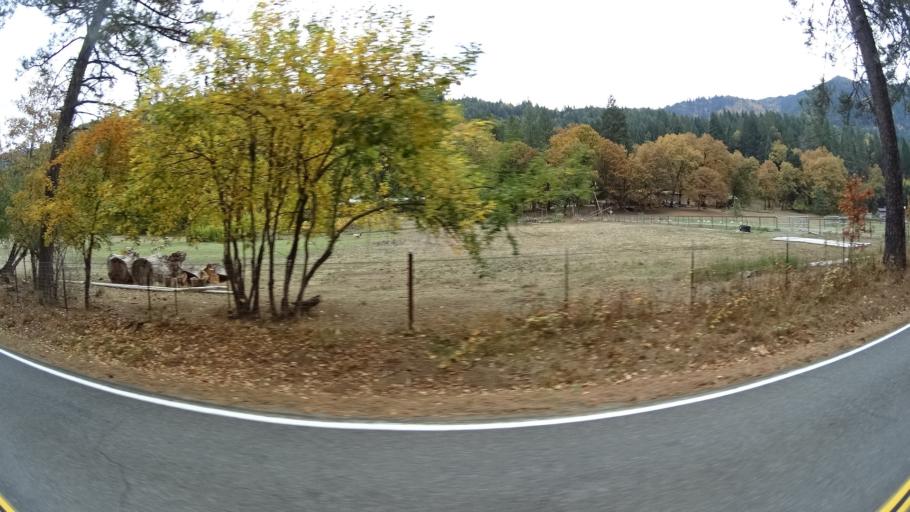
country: US
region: California
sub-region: Siskiyou County
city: Happy Camp
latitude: 41.8366
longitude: -123.3831
